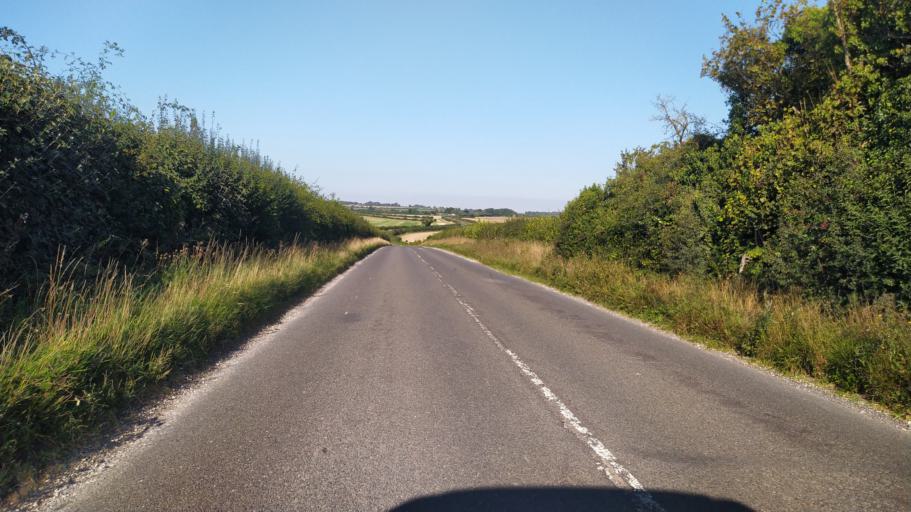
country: GB
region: England
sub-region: Hampshire
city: Abbotts Ann
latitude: 51.1622
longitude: -1.5817
